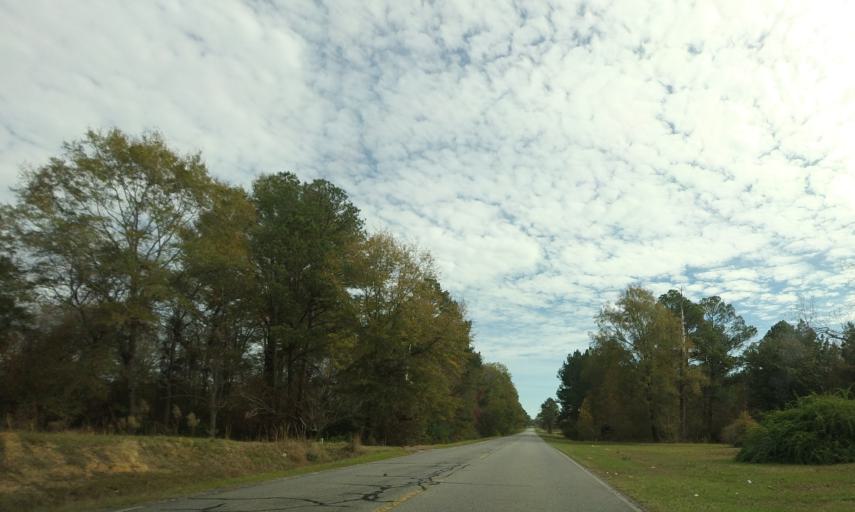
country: US
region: Georgia
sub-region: Bleckley County
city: Cochran
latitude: 32.3997
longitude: -83.2964
